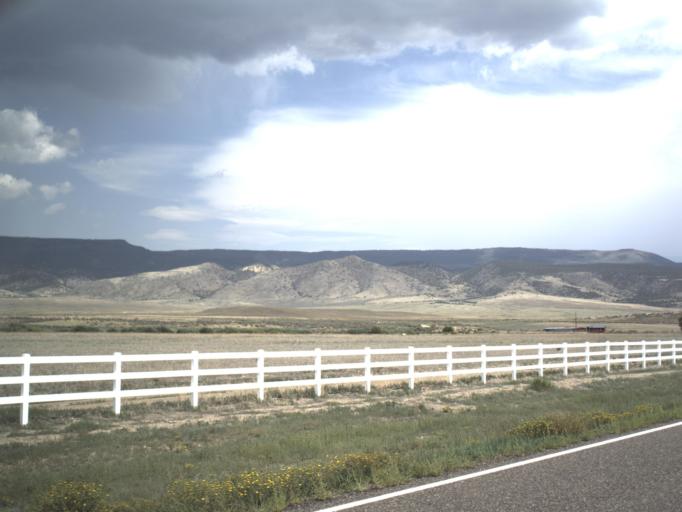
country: US
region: Utah
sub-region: Piute County
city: Junction
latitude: 38.1628
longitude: -112.0123
